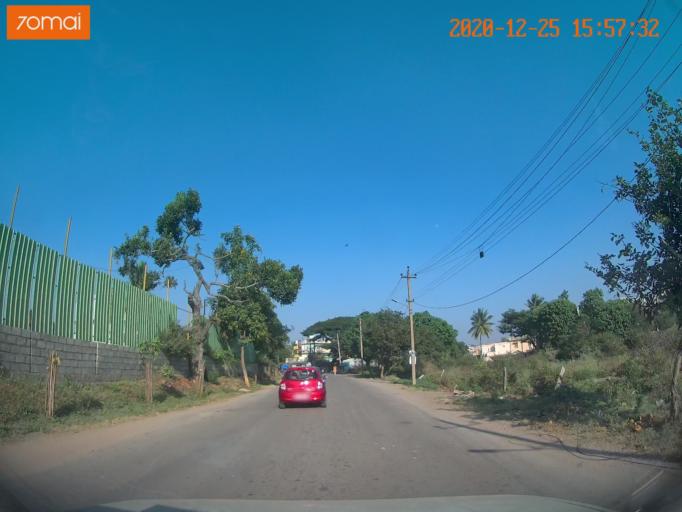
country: IN
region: Karnataka
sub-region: Bangalore Urban
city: Bangalore
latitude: 12.8698
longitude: 77.6233
